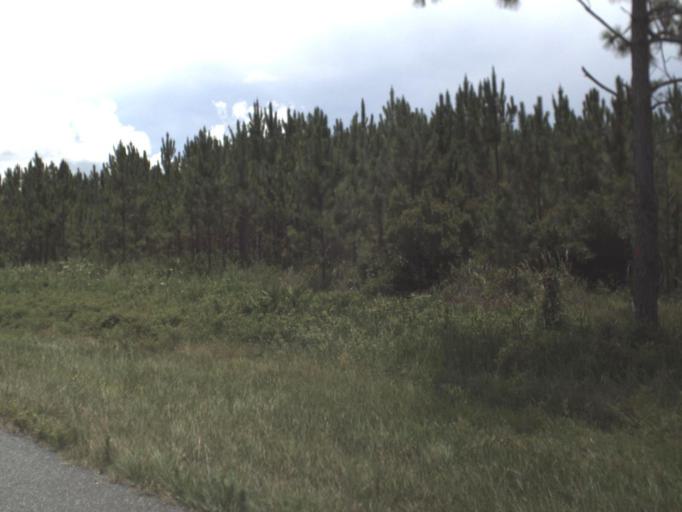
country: US
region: Florida
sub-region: Taylor County
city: Perry
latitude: 30.1428
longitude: -83.8306
